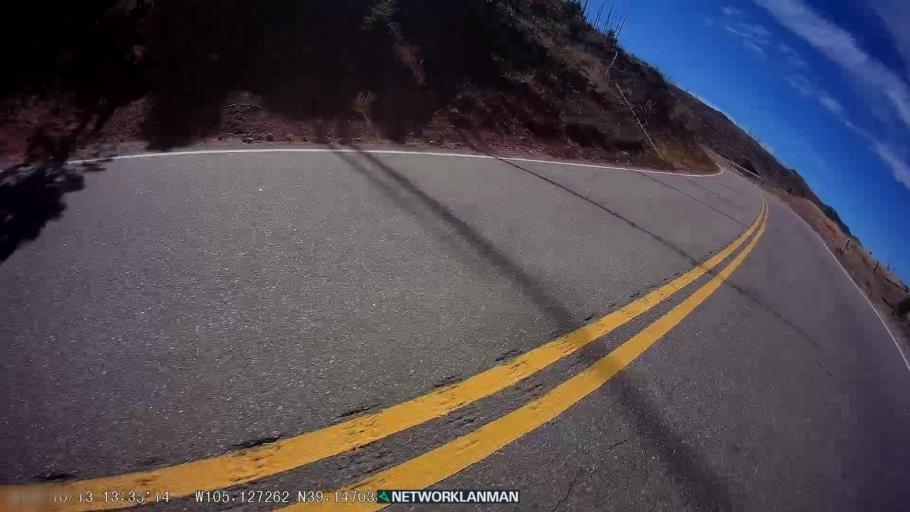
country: US
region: Colorado
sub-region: Teller County
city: Woodland Park
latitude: 39.1471
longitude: -105.1275
